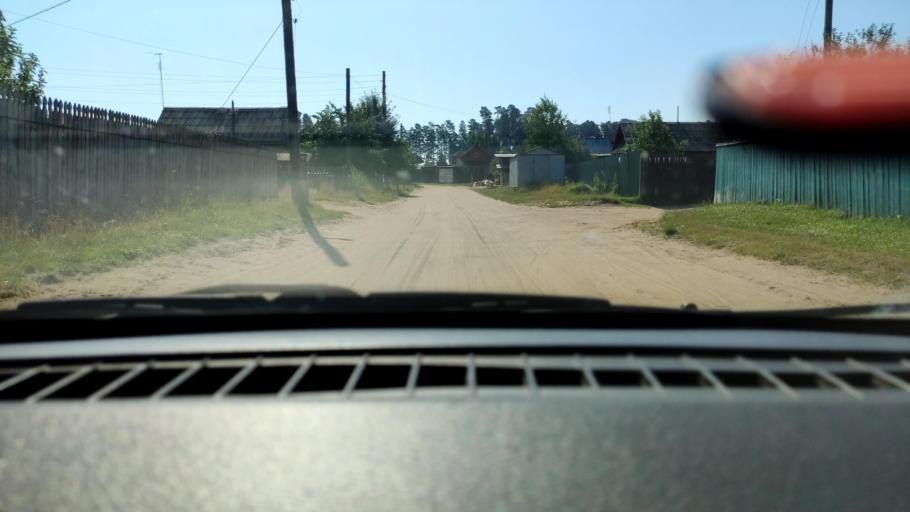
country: RU
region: Perm
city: Ust'-Kachka
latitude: 57.9327
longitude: 55.5160
